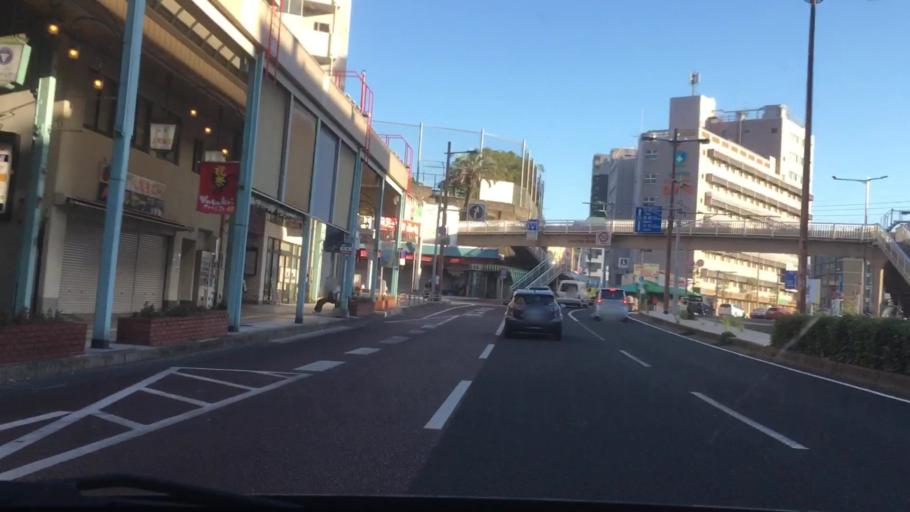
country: JP
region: Nagasaki
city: Sasebo
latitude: 33.1694
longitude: 129.7237
